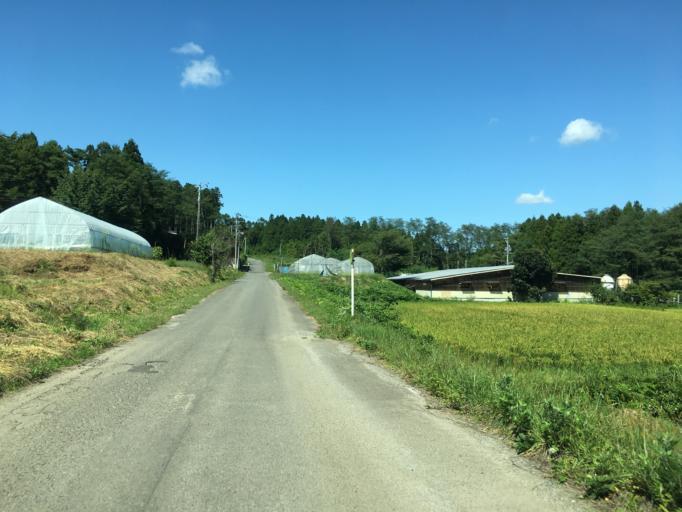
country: JP
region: Fukushima
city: Ishikawa
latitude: 37.2639
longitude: 140.5509
